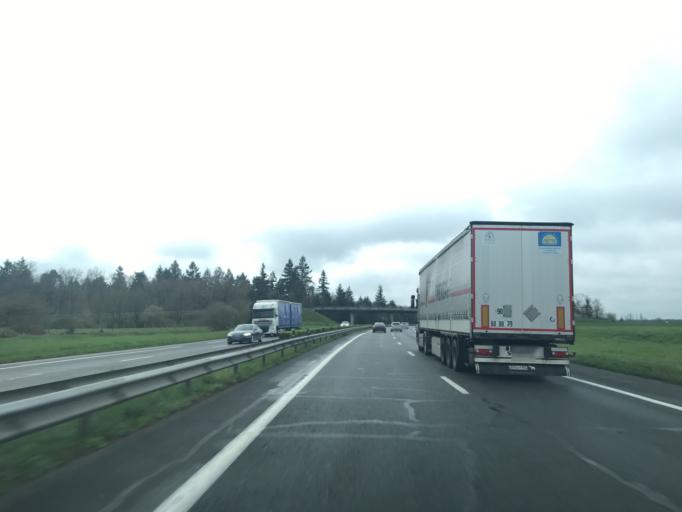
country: FR
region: Centre
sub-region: Departement du Loiret
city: Chateauneuf-sur-Loire
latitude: 47.8830
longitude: 2.2277
